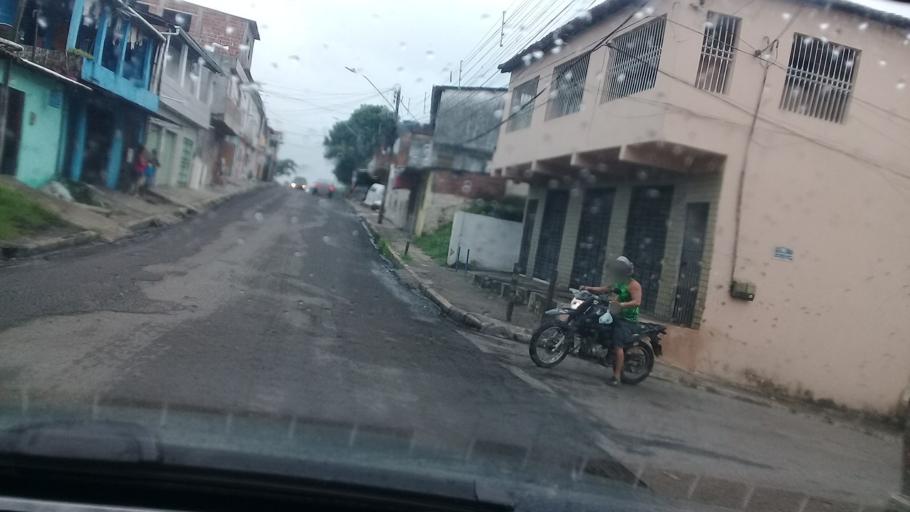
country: BR
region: Pernambuco
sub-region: Jaboatao Dos Guararapes
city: Jaboatao dos Guararapes
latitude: -8.0840
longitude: -34.9785
